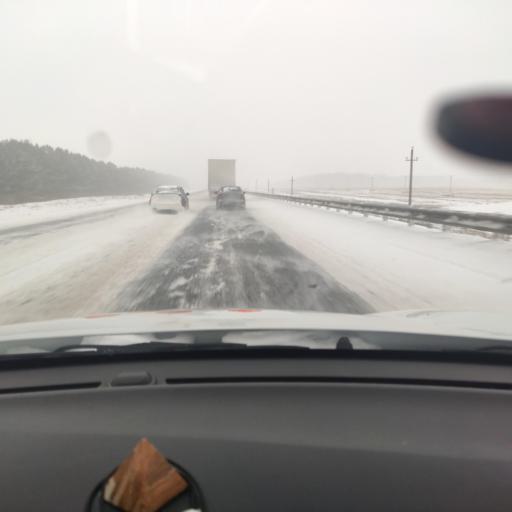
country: RU
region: Tatarstan
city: Sviyazhsk
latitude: 55.7277
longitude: 48.8140
